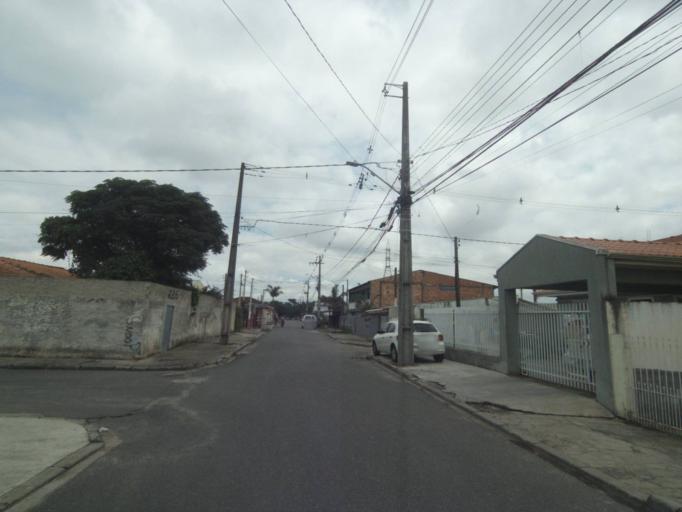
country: BR
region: Parana
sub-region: Pinhais
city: Pinhais
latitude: -25.4638
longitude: -49.1948
